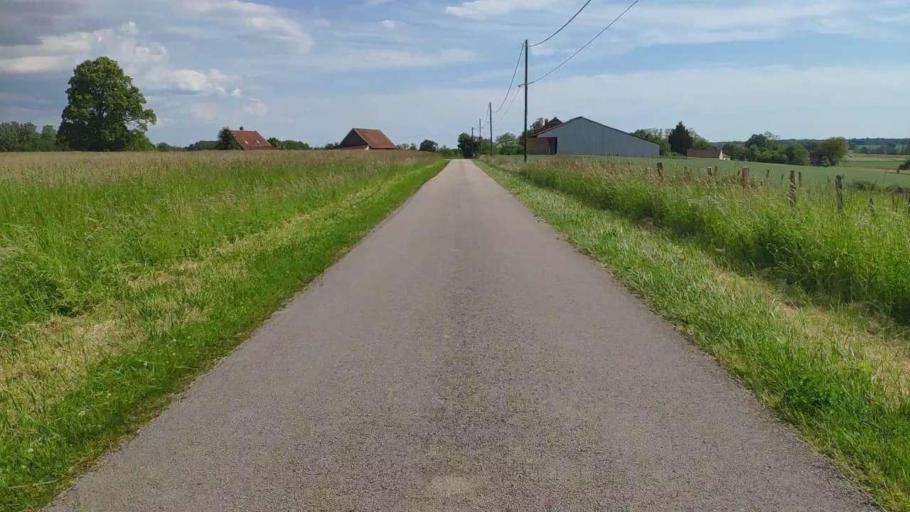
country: FR
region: Franche-Comte
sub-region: Departement du Jura
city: Bletterans
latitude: 46.8151
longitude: 5.3794
